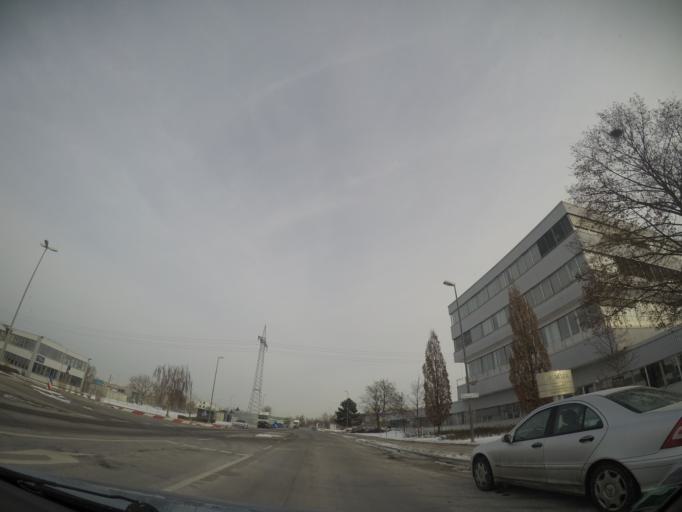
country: DE
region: Bavaria
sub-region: Swabia
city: Neu-Ulm
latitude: 48.3884
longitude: 10.0363
